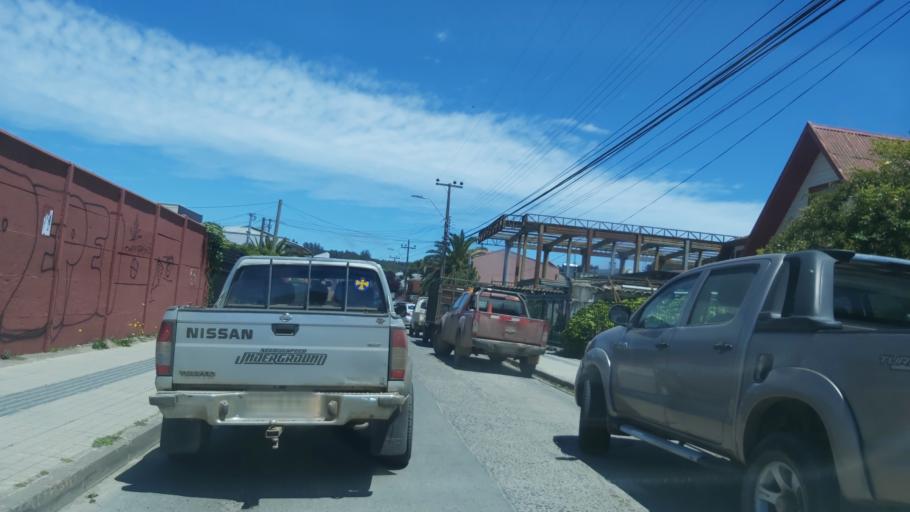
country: CL
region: Maule
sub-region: Provincia de Talca
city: Constitucion
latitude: -35.3285
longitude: -72.4087
